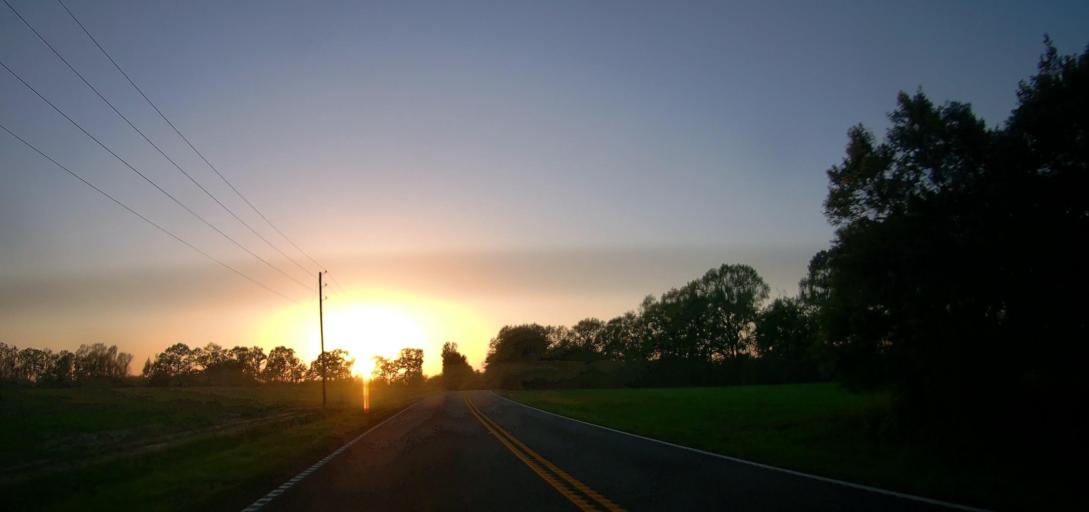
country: US
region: Georgia
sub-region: Marion County
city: Buena Vista
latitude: 32.3702
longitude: -84.5478
